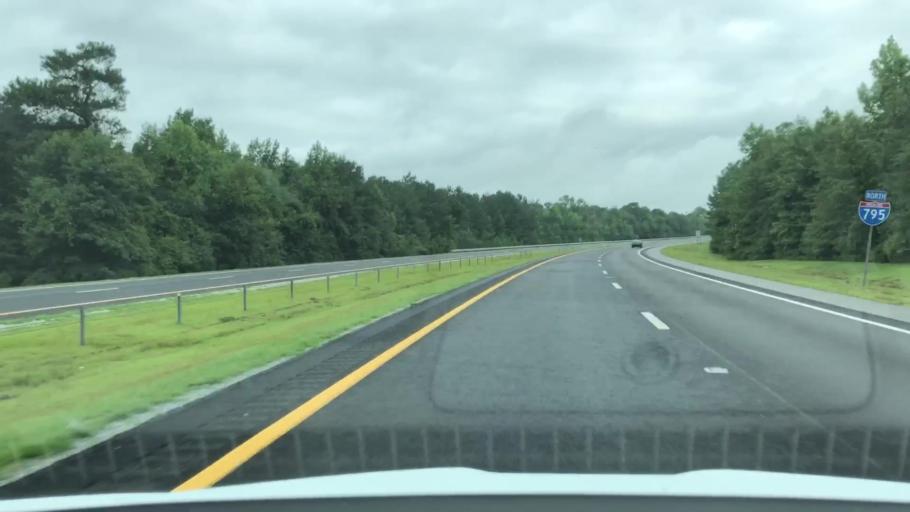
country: US
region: North Carolina
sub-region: Wayne County
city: Fremont
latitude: 35.5022
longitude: -77.9995
